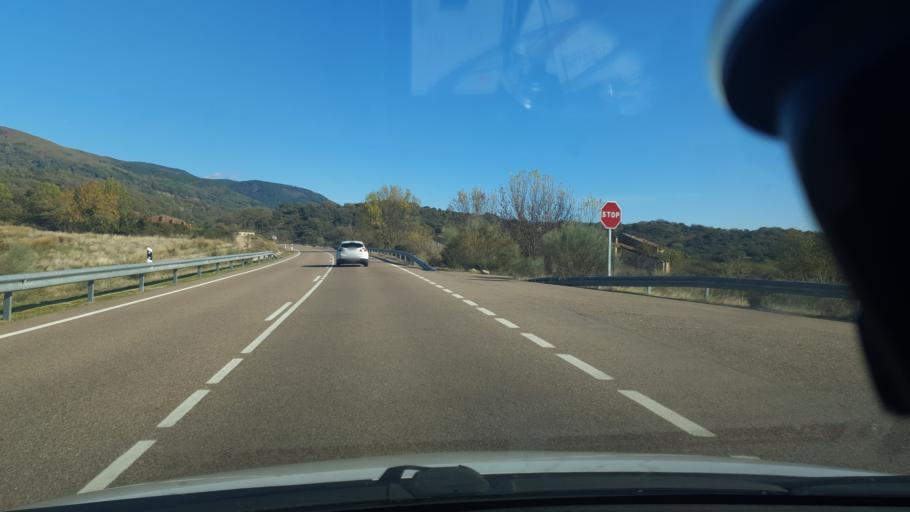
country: ES
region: Castille and Leon
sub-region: Provincia de Avila
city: Poyales del Hoyo
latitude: 40.1467
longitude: -5.1925
